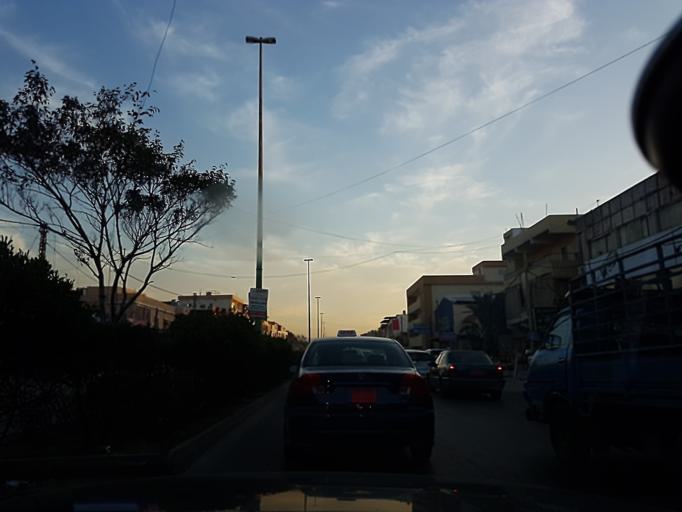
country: LB
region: Beyrouth
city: Beirut
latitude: 33.8408
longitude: 35.4848
